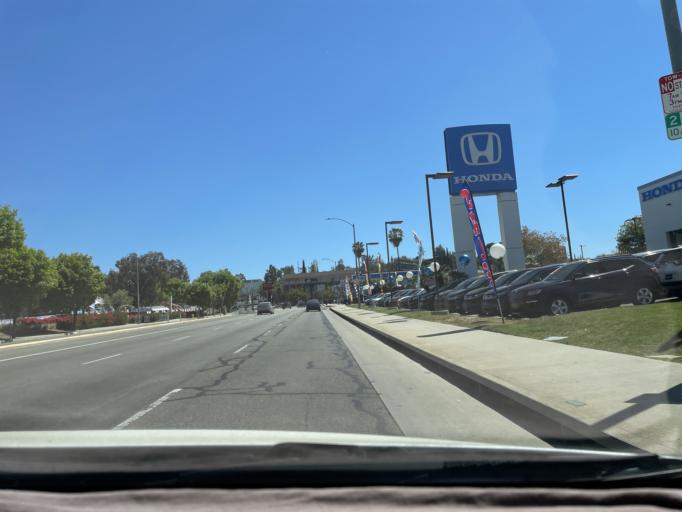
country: US
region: California
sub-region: Los Angeles County
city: Woodland Hills
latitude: 34.1820
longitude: -118.6060
